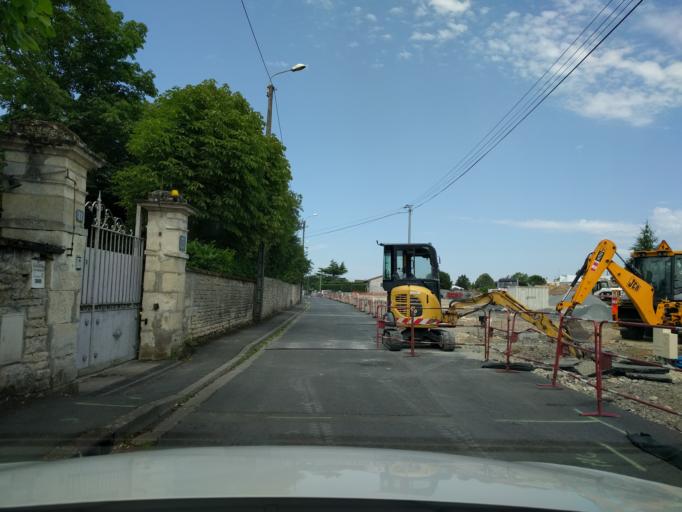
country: FR
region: Poitou-Charentes
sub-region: Departement des Deux-Sevres
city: Niort
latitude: 46.3377
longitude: -0.4824
